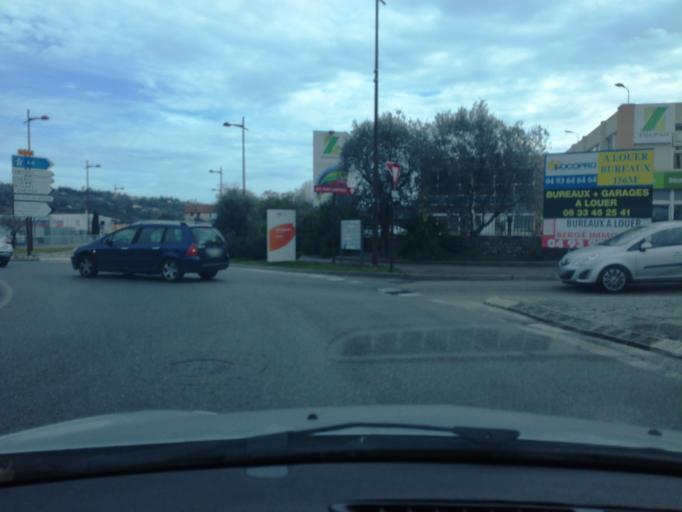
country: FR
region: Provence-Alpes-Cote d'Azur
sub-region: Departement des Alpes-Maritimes
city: Grasse
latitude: 43.6536
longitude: 6.9441
